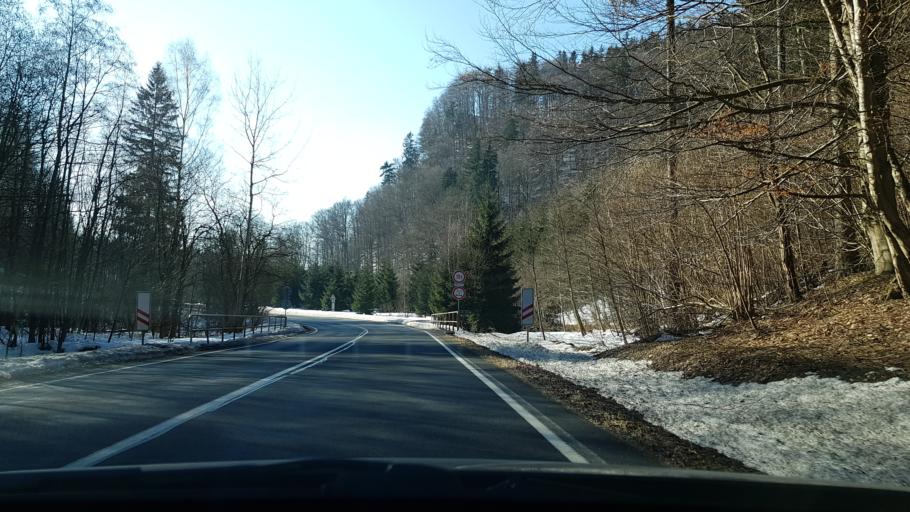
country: CZ
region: Olomoucky
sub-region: Okres Sumperk
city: Stare Mesto
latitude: 50.1375
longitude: 17.0121
